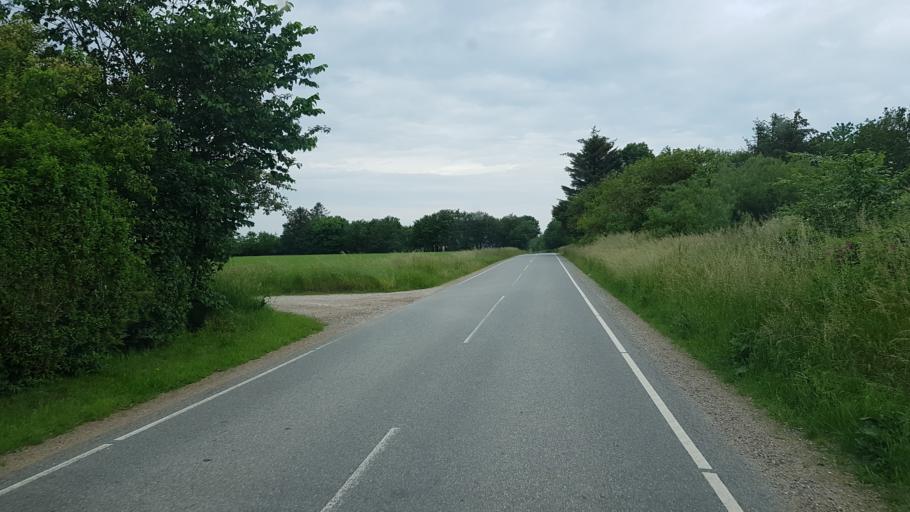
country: DK
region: South Denmark
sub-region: Varde Kommune
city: Oksbol
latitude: 55.6736
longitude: 8.3099
